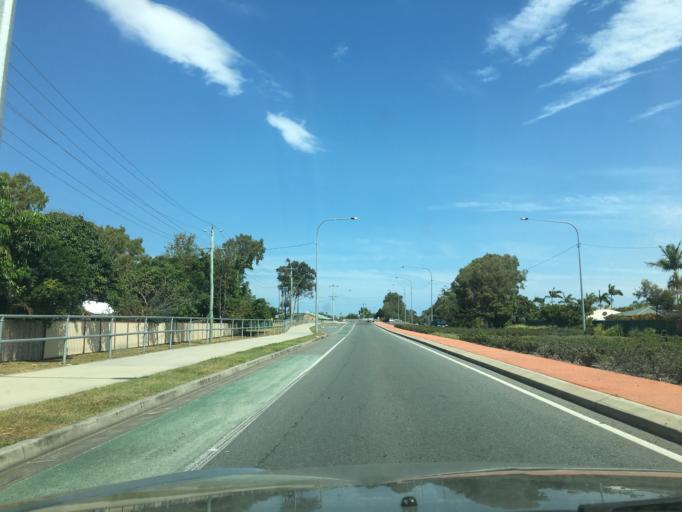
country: AU
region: Queensland
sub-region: Moreton Bay
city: Bongaree
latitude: -27.0687
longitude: 153.1610
